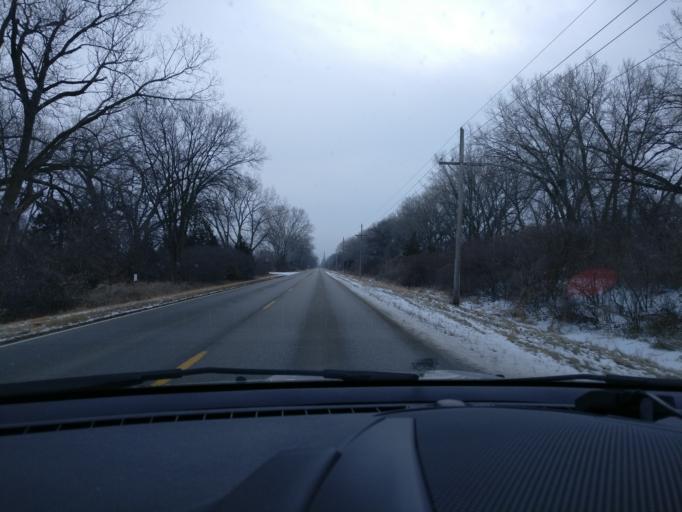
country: US
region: Nebraska
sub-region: Dodge County
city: Fremont
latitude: 41.4448
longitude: -96.5427
